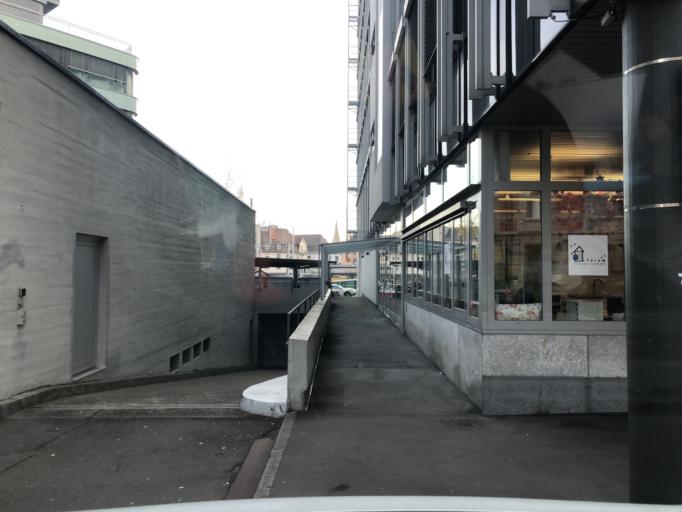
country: CH
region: Aargau
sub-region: Bezirk Baden
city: Baden
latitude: 47.4760
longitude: 8.3060
